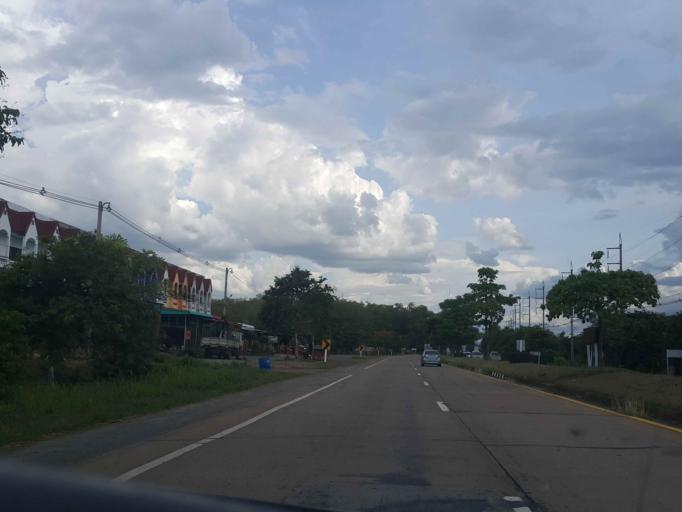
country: TH
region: Phrae
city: Den Chai
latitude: 17.9911
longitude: 100.0977
